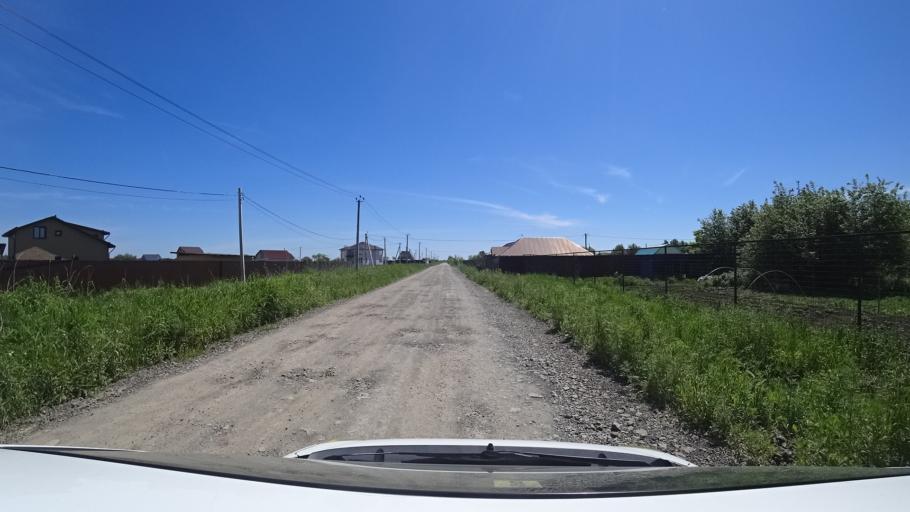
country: RU
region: Khabarovsk Krai
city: Topolevo
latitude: 48.5111
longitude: 135.1943
